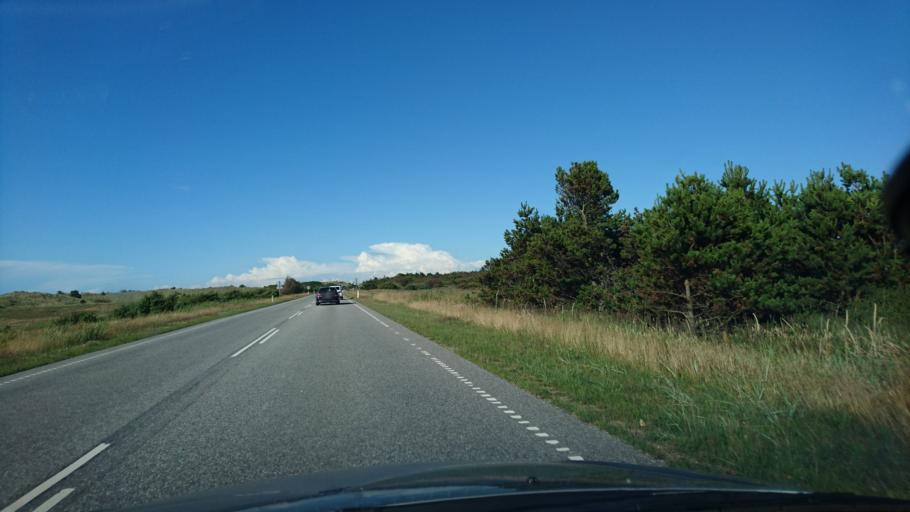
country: DK
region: North Denmark
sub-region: Frederikshavn Kommune
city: Skagen
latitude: 57.7223
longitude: 10.5402
